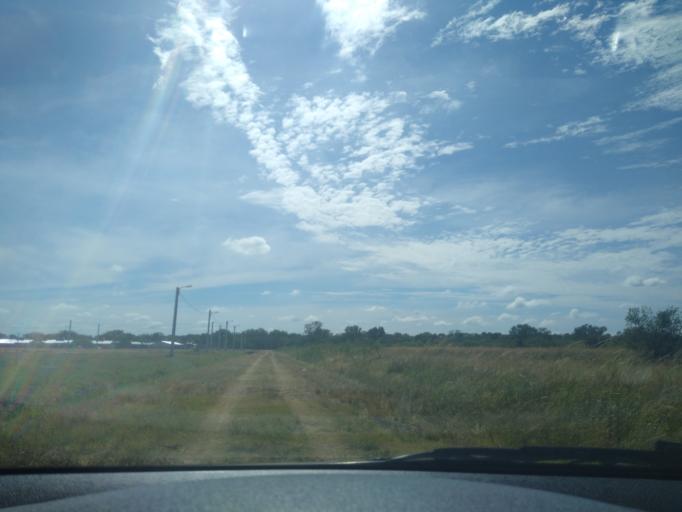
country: AR
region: Chaco
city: Resistencia
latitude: -27.4160
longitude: -58.9582
